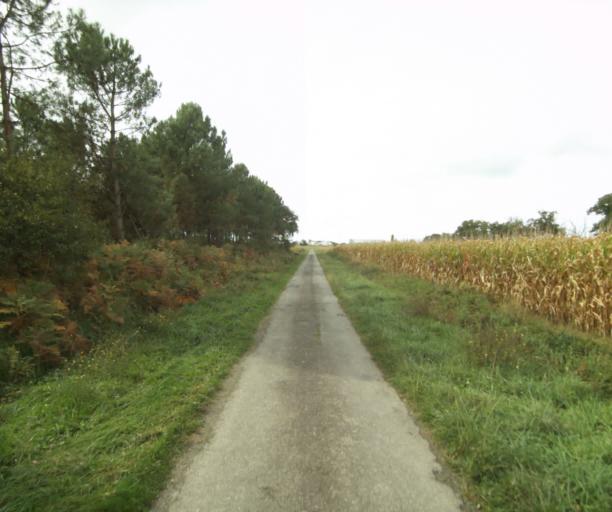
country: FR
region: Midi-Pyrenees
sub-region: Departement du Gers
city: Eauze
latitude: 43.8396
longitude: 0.0989
